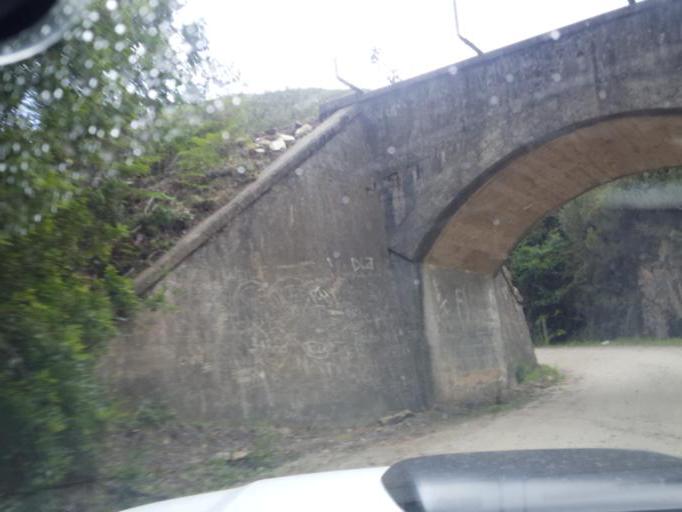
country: ZA
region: Western Cape
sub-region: Eden District Municipality
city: George
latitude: -33.8865
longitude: 22.4314
